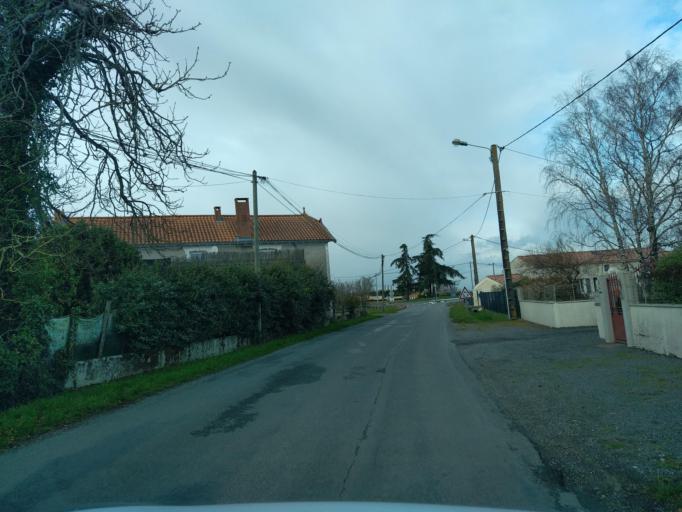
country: FR
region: Pays de la Loire
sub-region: Departement de la Vendee
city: Vix
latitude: 46.3524
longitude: -0.8408
